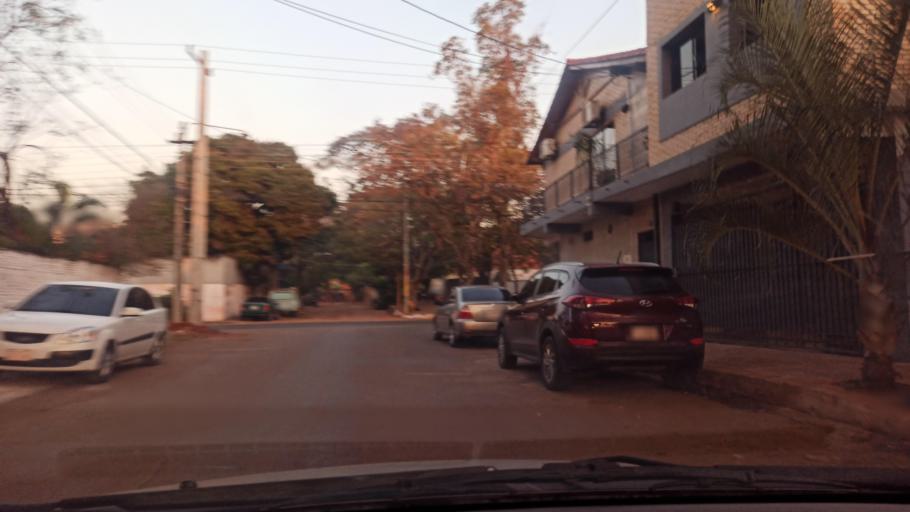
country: PY
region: Central
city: Fernando de la Mora
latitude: -25.3243
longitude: -57.5632
